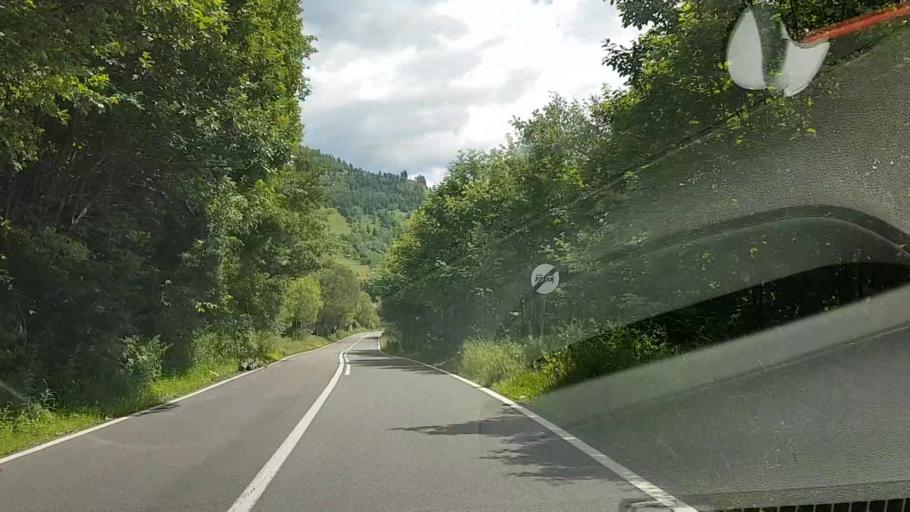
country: RO
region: Suceava
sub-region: Comuna Crucea
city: Crucea
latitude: 47.3934
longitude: 25.5688
